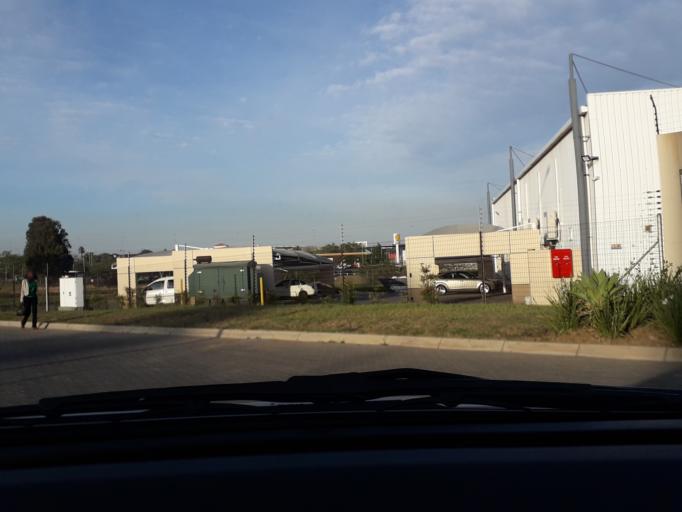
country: ZA
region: Gauteng
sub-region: City of Johannesburg Metropolitan Municipality
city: Midrand
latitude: -25.9291
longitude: 28.1481
